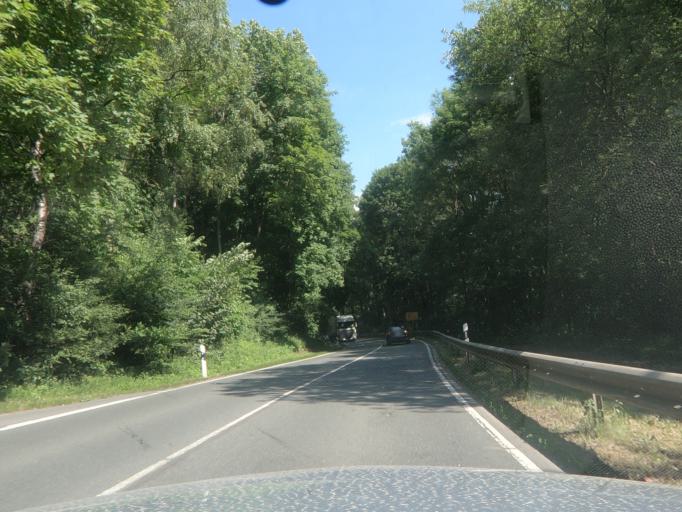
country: DE
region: North Rhine-Westphalia
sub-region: Regierungsbezirk Arnsberg
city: Finnentrop
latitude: 51.1458
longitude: 8.0168
